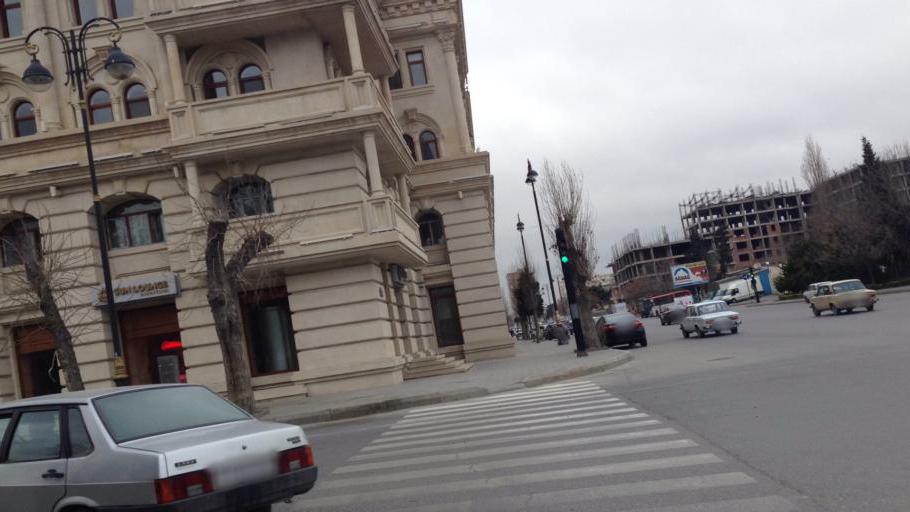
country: AZ
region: Baki
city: Baku
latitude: 40.3926
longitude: 49.8451
